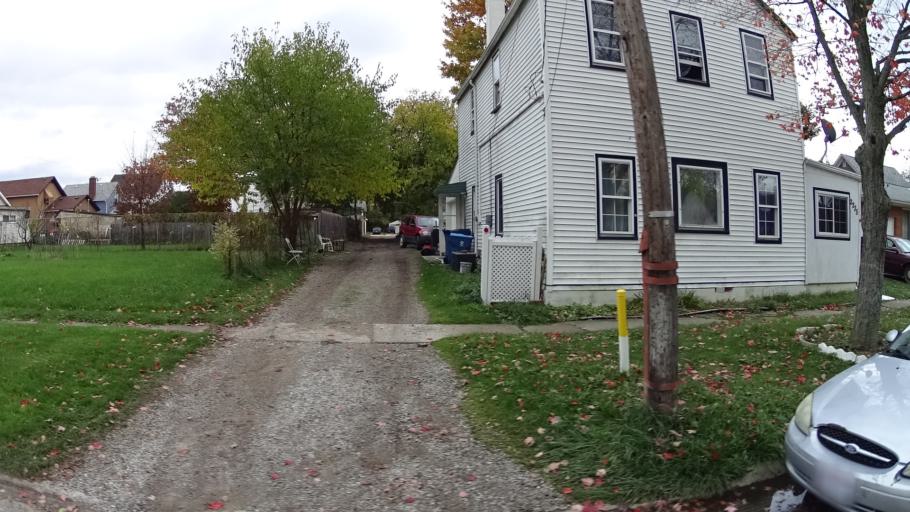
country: US
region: Ohio
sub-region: Lorain County
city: Lorain
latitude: 41.4495
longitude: -82.1699
